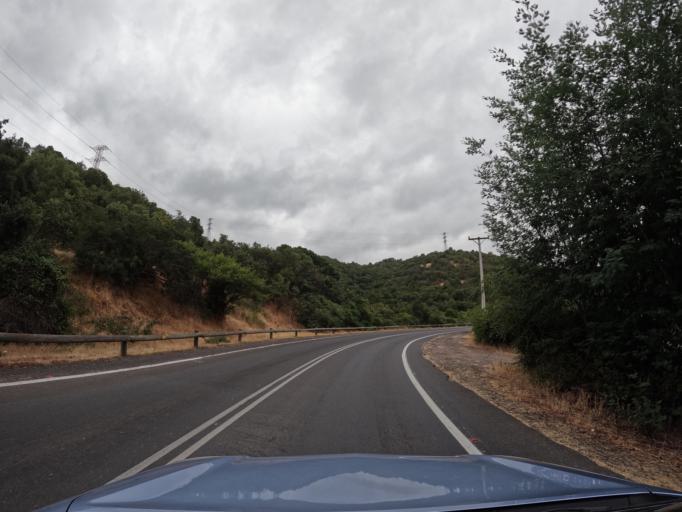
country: CL
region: O'Higgins
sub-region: Provincia de Colchagua
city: Chimbarongo
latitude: -34.7283
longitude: -71.1047
